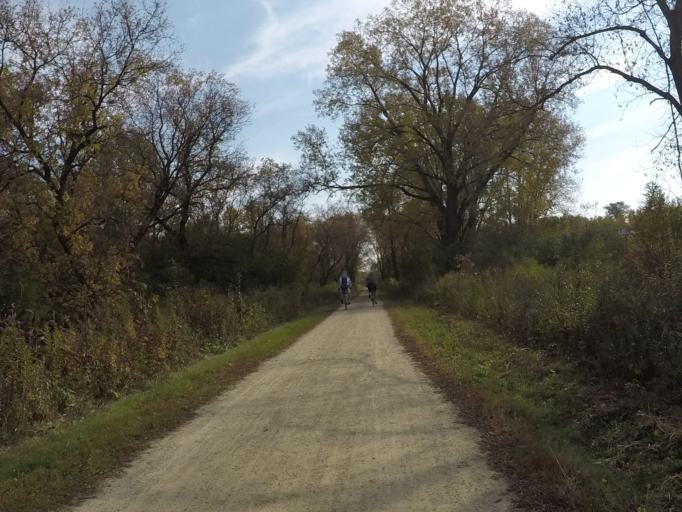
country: US
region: Wisconsin
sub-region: Dane County
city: Cross Plains
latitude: 43.0247
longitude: -89.6257
